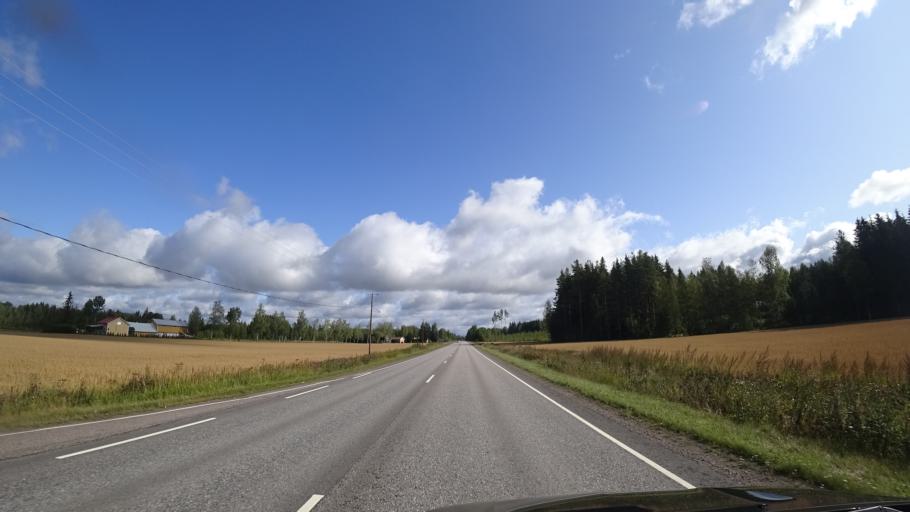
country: FI
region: Uusimaa
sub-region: Helsinki
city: Hyvinge
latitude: 60.5406
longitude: 24.9286
